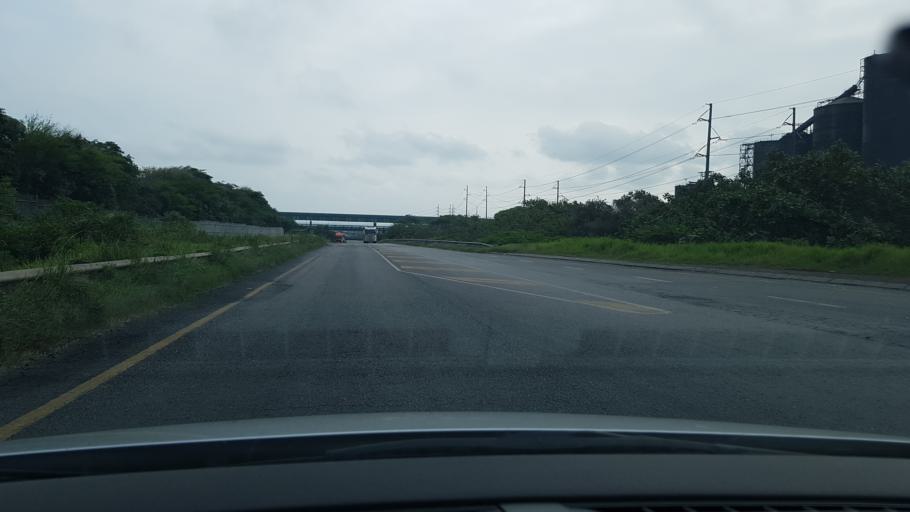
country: ZA
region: KwaZulu-Natal
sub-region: uThungulu District Municipality
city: Richards Bay
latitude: -28.7750
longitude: 32.0319
